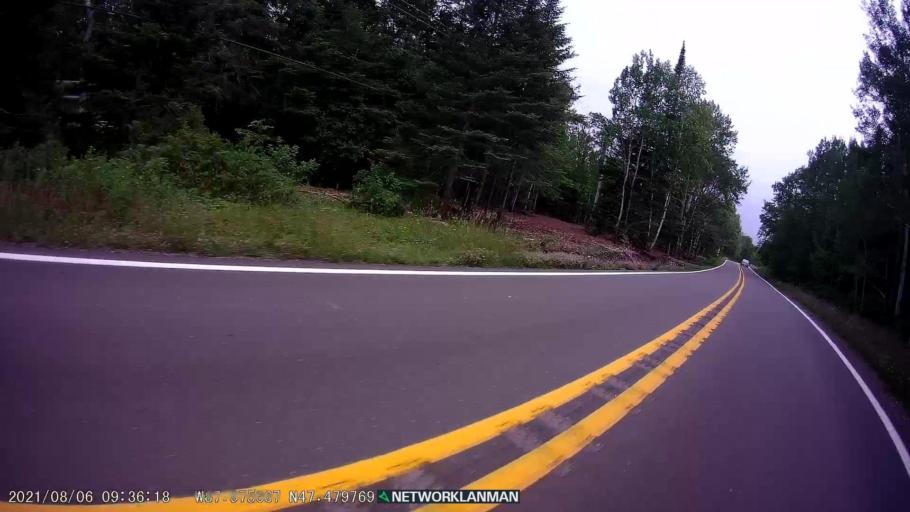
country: US
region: Michigan
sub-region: Keweenaw County
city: Eagle River
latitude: 47.4796
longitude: -87.9766
